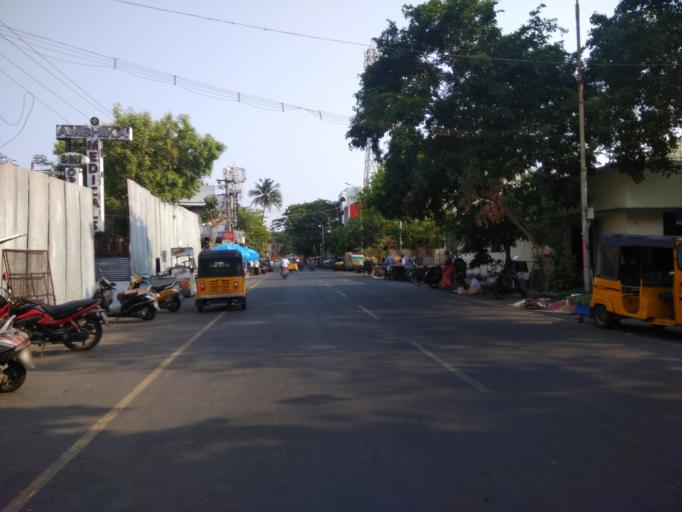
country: IN
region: Tamil Nadu
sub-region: Kancheepuram
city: Saint Thomas Mount
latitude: 12.9845
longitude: 80.1885
